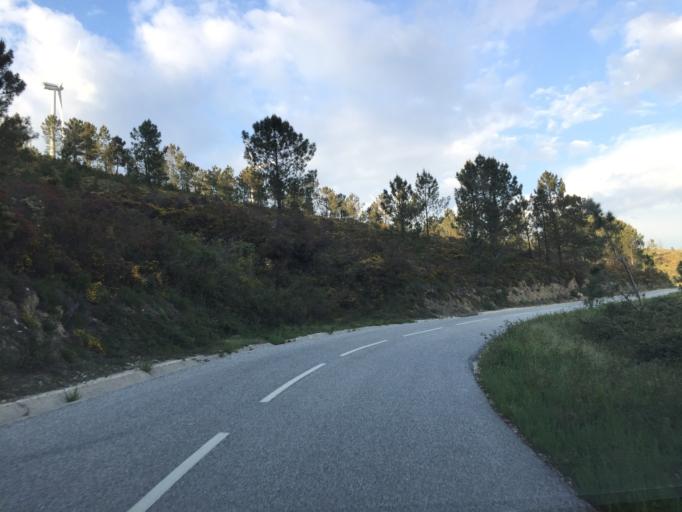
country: PT
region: Coimbra
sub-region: Pampilhosa da Serra
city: Pampilhosa da Serra
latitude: 40.1111
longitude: -8.0101
